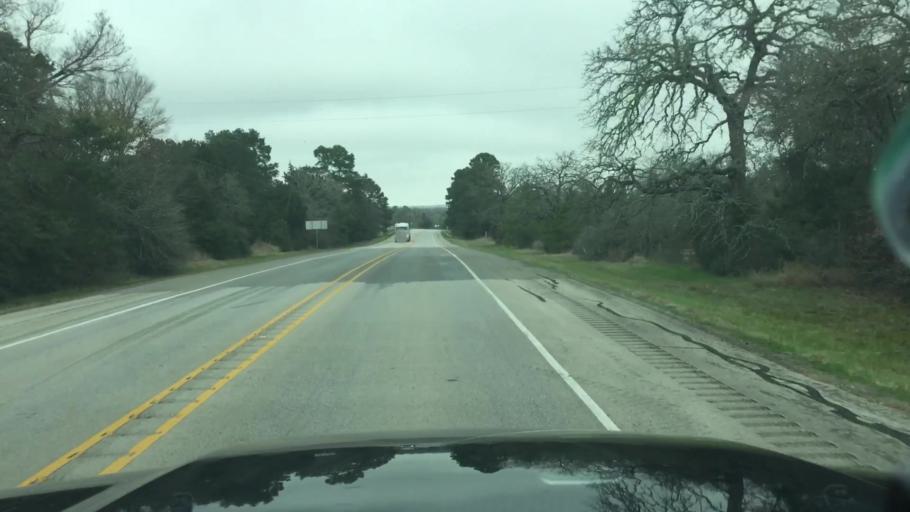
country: US
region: Texas
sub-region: Lee County
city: Giddings
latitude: 30.0777
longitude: -96.9171
